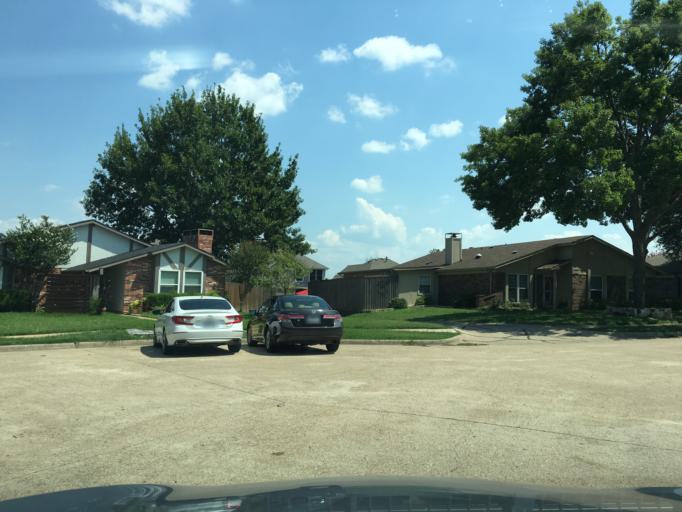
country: US
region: Texas
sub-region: Collin County
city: Plano
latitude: 32.9674
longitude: -96.6675
